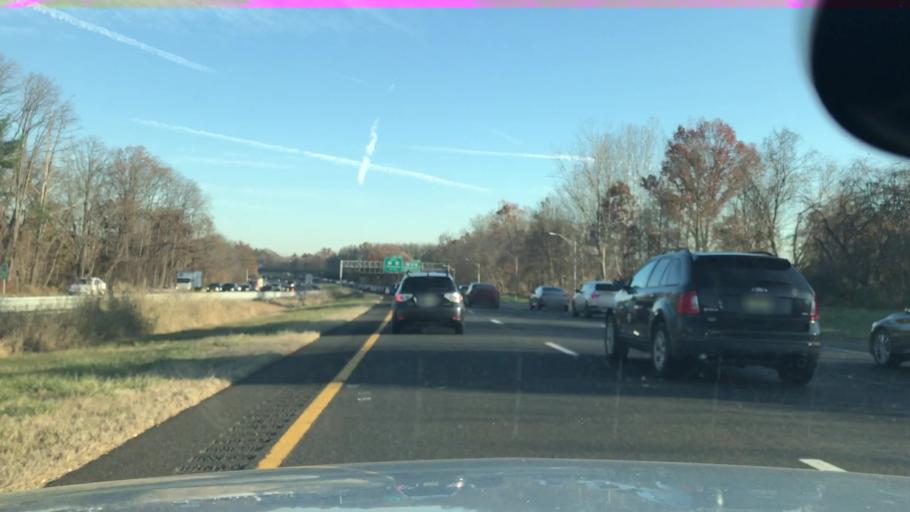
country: US
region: New Jersey
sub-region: Burlington County
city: Bordentown
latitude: 40.1207
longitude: -74.7196
